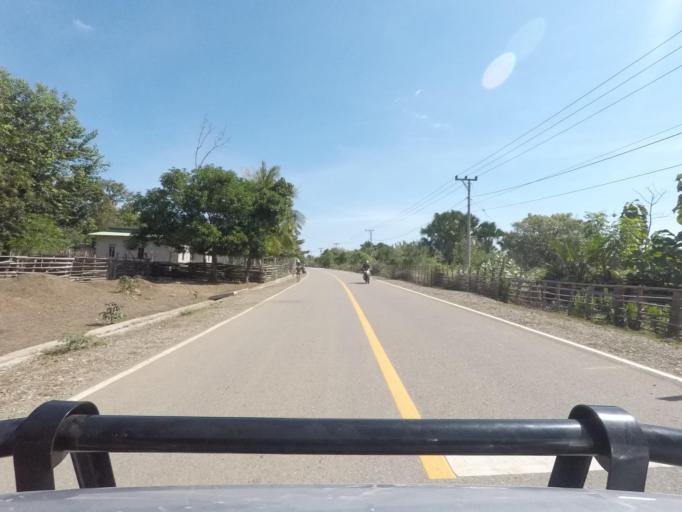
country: TL
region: Bobonaro
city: Maliana
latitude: -8.8807
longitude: 125.0318
